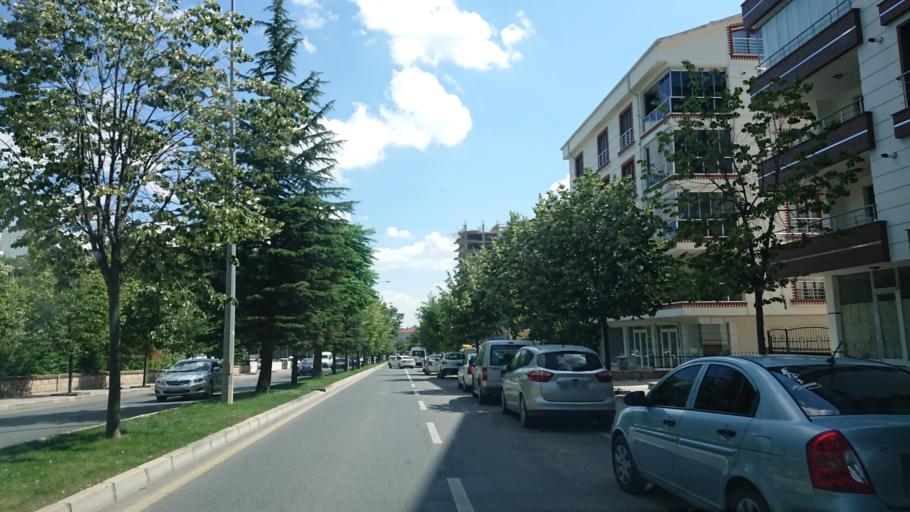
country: TR
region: Kirsehir
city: Kirsehir
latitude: 39.1575
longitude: 34.1600
